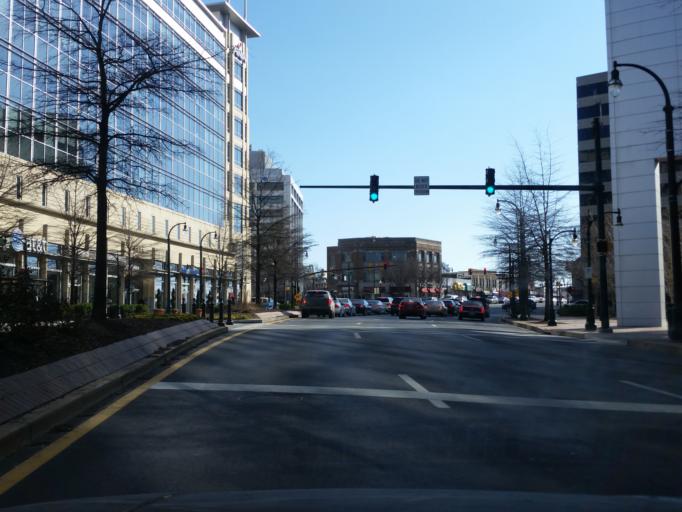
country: US
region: Maryland
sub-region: Montgomery County
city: Silver Spring
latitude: 38.9954
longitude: -77.0276
